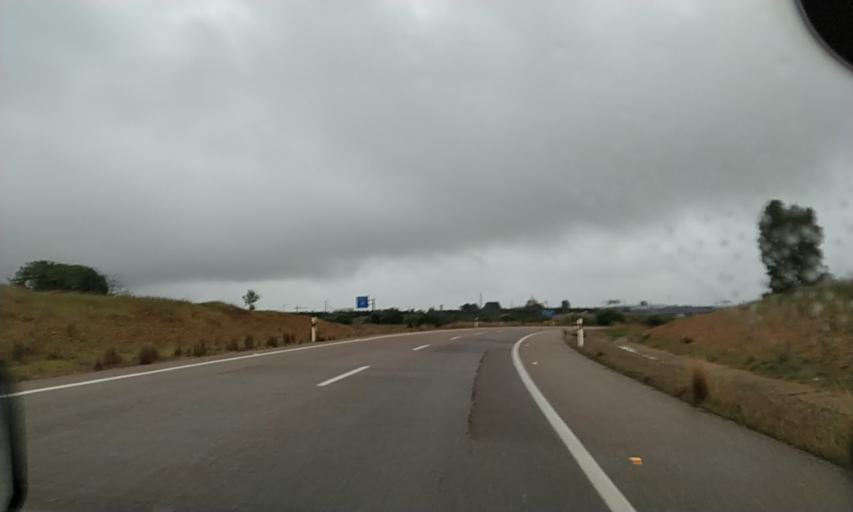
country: ES
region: Extremadura
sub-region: Provincia de Badajoz
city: Calamonte
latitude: 38.9081
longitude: -6.3790
